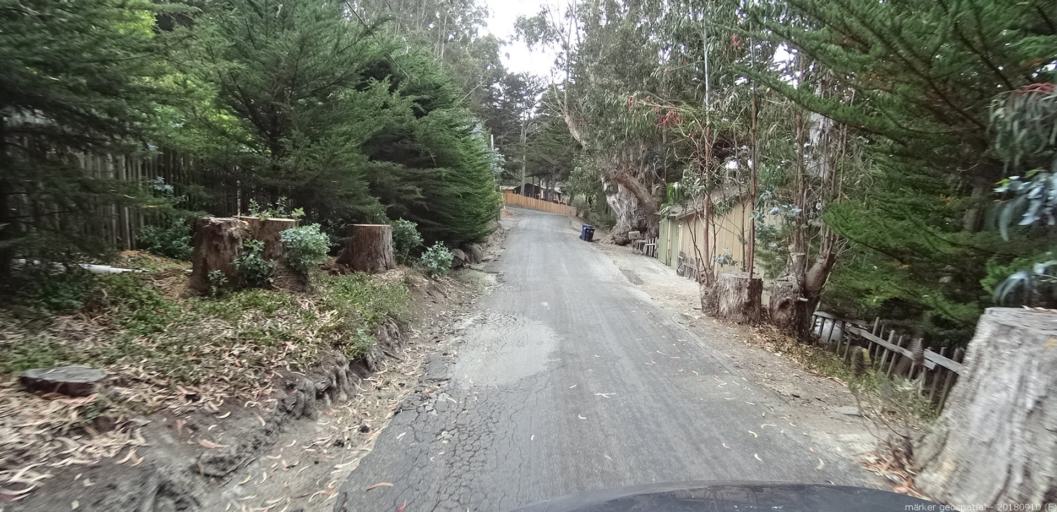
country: US
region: California
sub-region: Monterey County
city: Carmel-by-the-Sea
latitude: 36.4932
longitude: -121.9362
